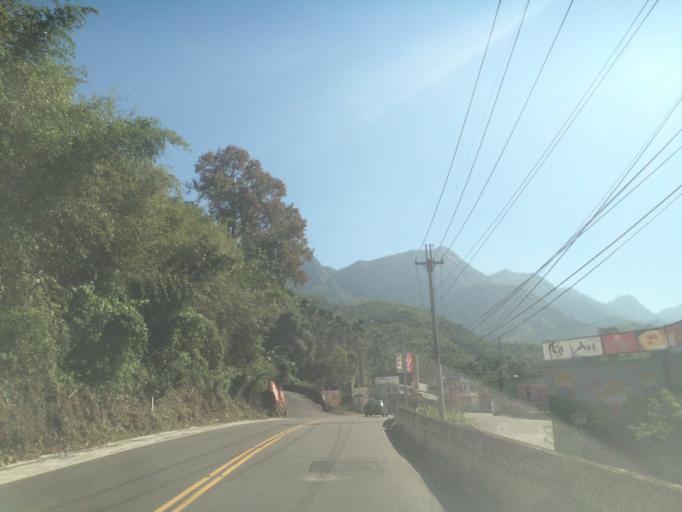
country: TW
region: Taiwan
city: Lugu
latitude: 23.7295
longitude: 120.7741
